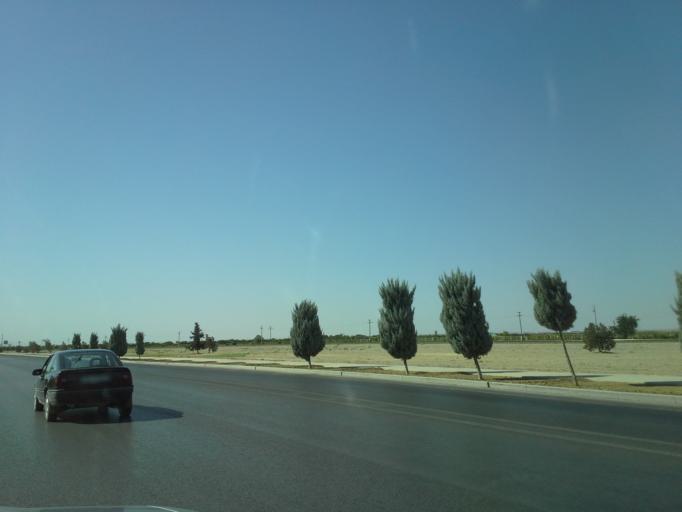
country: TM
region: Ahal
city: Annau
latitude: 37.9141
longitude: 58.4814
